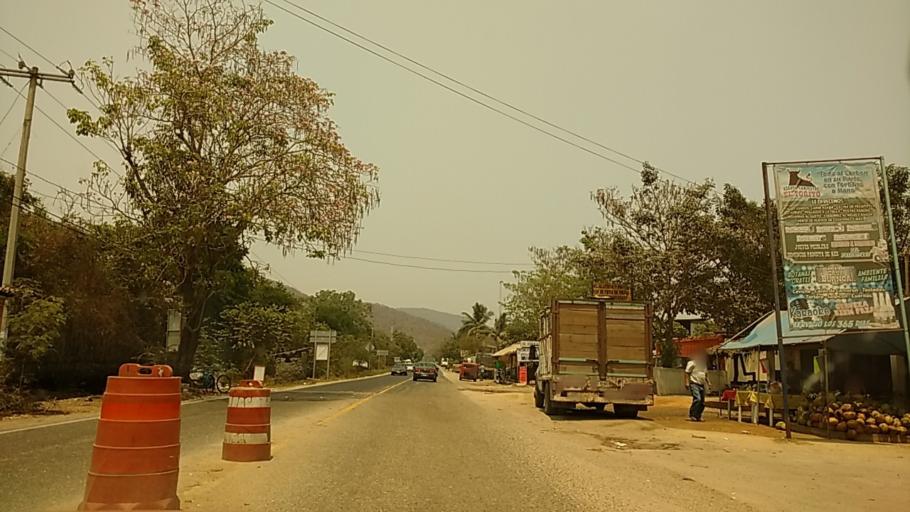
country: MX
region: Guerrero
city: Bajos del Ejido
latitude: 16.9622
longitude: -99.9766
